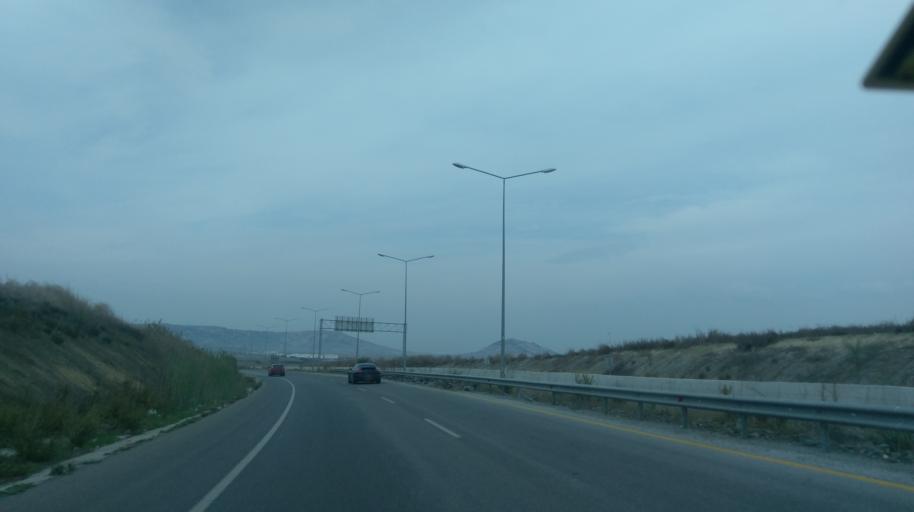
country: CY
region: Lefkosia
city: Mammari
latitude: 35.2181
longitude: 33.1779
